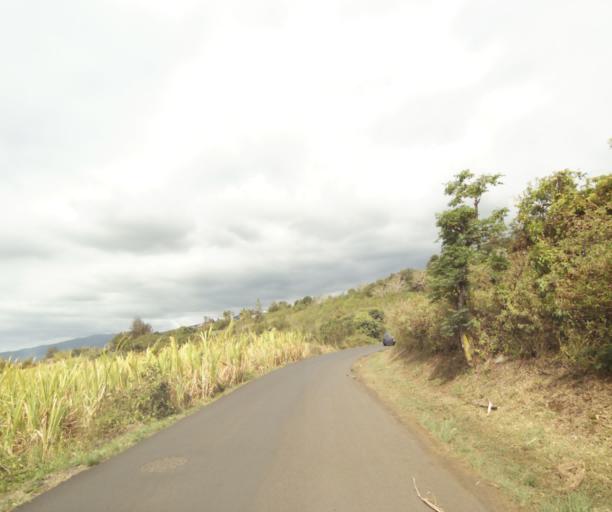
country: RE
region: Reunion
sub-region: Reunion
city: Saint-Paul
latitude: -21.0330
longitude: 55.2917
